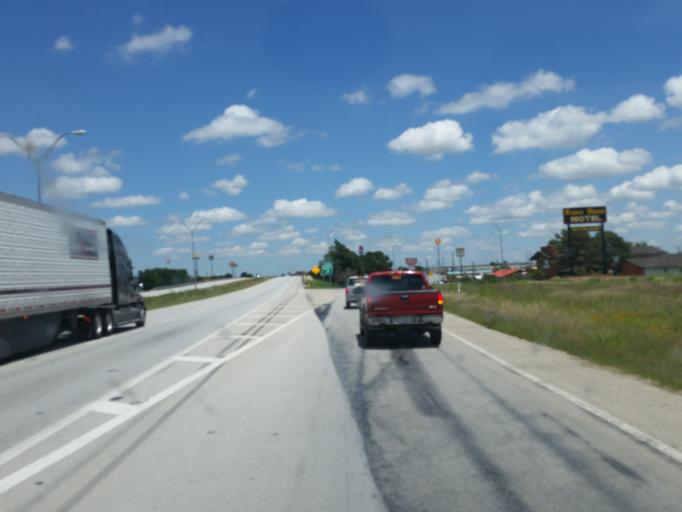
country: US
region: Texas
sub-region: Nolan County
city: Sweetwater
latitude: 32.4492
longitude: -100.4024
